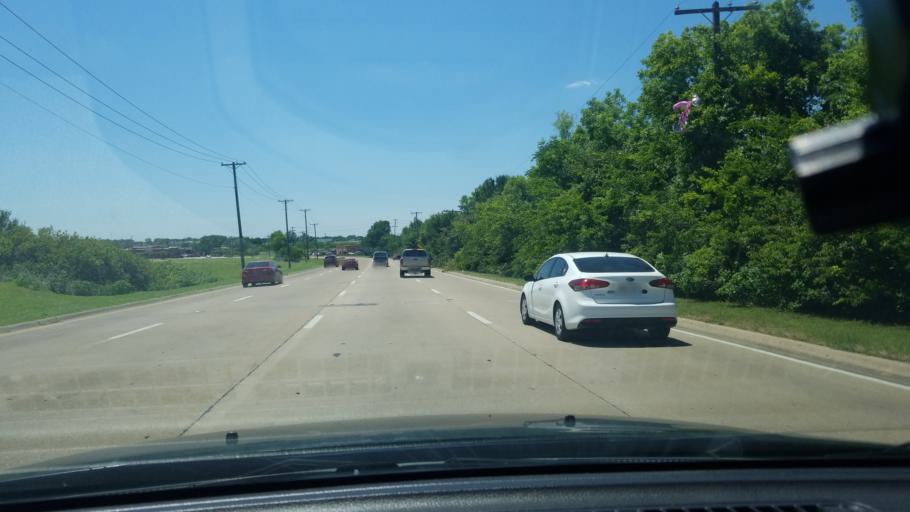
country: US
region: Texas
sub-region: Dallas County
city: Mesquite
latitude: 32.7693
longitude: -96.6153
